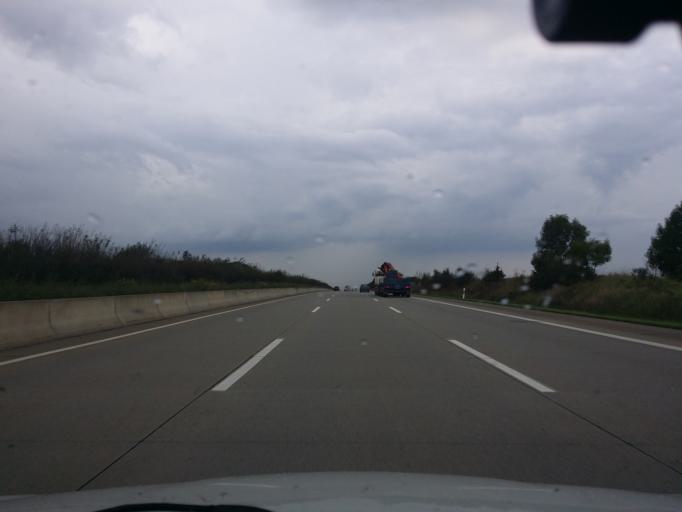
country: DE
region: Thuringia
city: Mellingen
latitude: 50.9126
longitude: 11.4143
